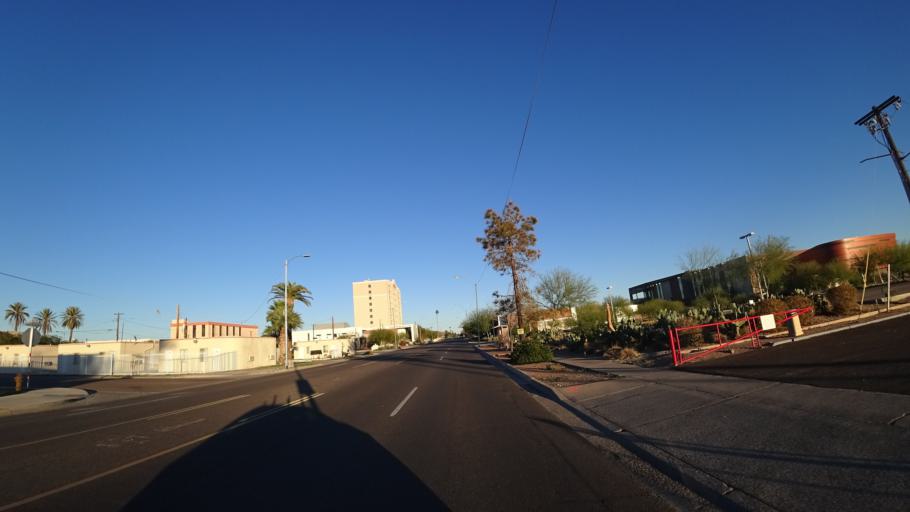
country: US
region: Arizona
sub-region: Maricopa County
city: Tempe Junction
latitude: 33.4512
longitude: -112.0000
